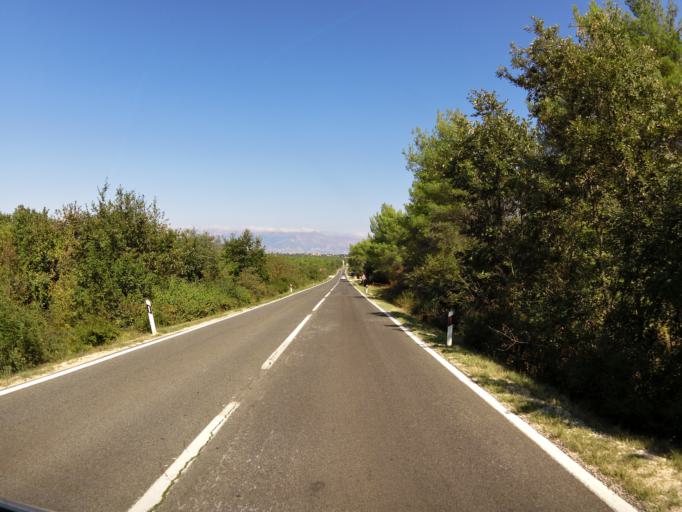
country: HR
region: Zadarska
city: Policnik
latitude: 44.1629
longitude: 15.3502
